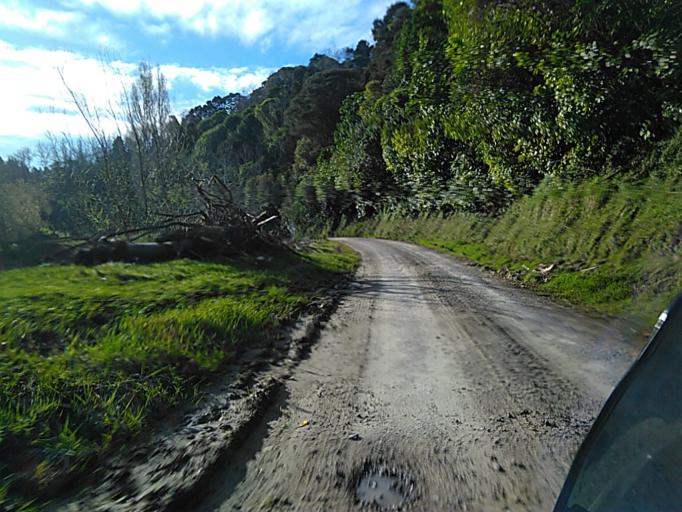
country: NZ
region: Gisborne
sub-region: Gisborne District
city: Gisborne
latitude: -38.5893
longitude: 178.0696
